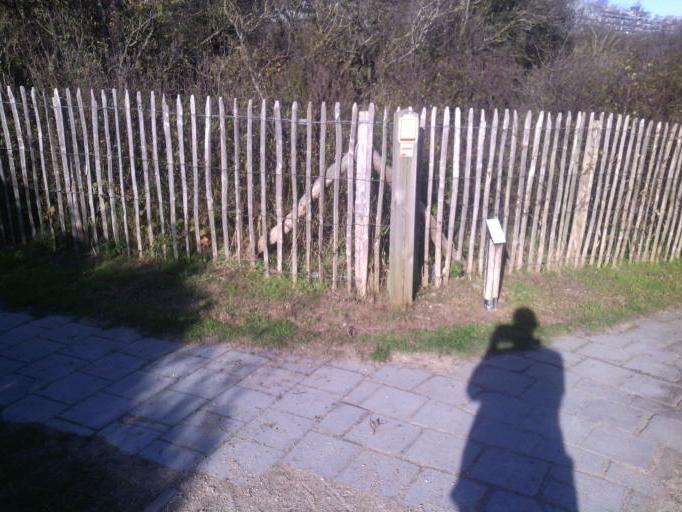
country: BE
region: Flanders
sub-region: Provincie West-Vlaanderen
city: Middelkerke
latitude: 51.1784
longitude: 2.7968
